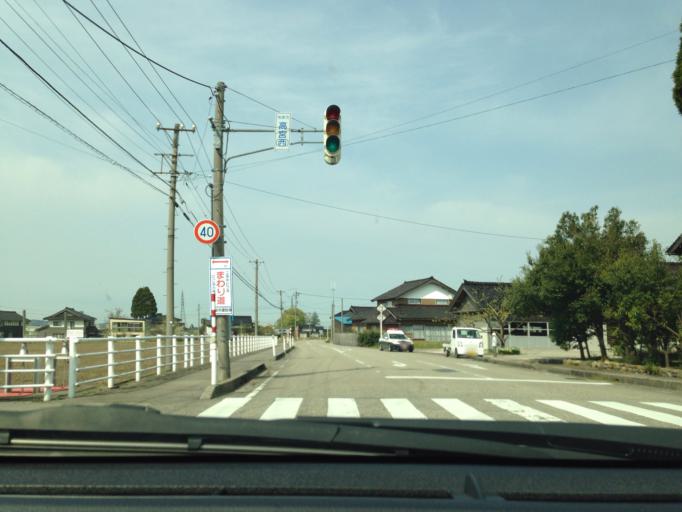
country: JP
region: Toyama
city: Fukumitsu
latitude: 36.5447
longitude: 136.8701
